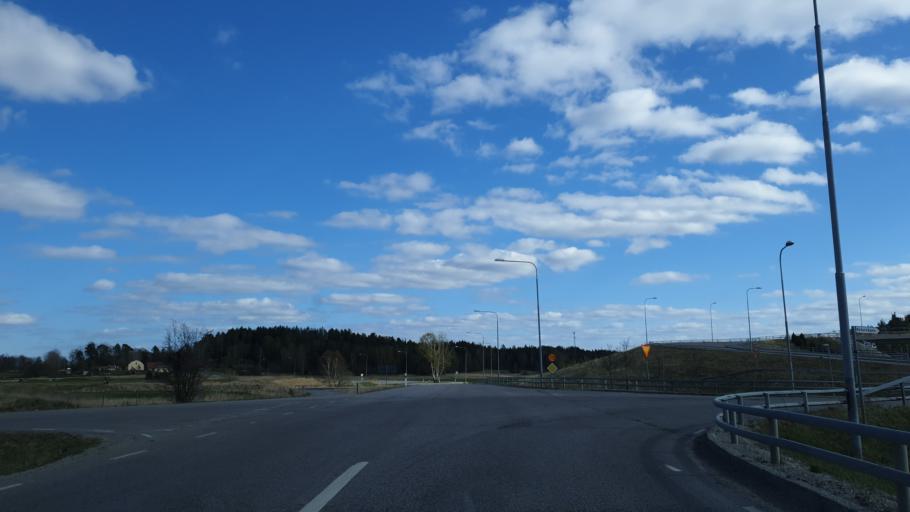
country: SE
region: Stockholm
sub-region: Sigtuna Kommun
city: Marsta
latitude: 59.6112
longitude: 17.8677
